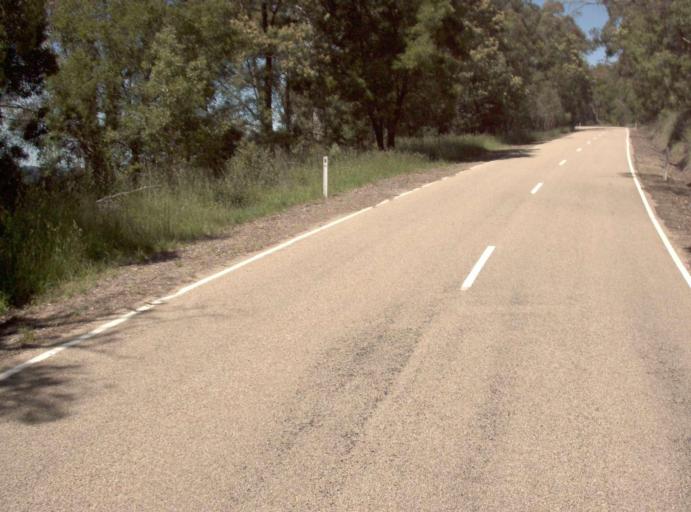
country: AU
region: Victoria
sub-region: East Gippsland
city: Lakes Entrance
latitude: -37.2436
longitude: 148.2559
